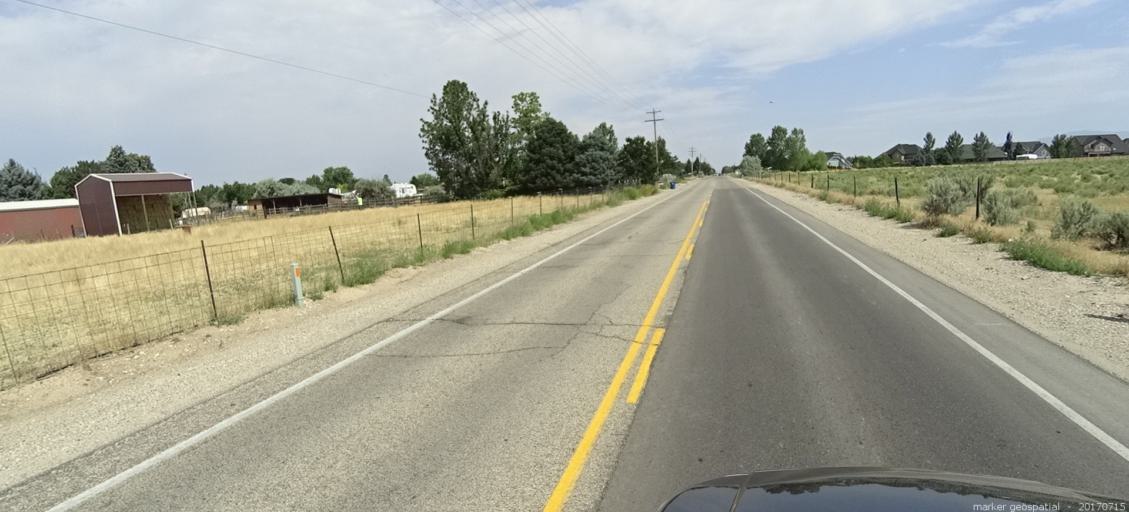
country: US
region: Idaho
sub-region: Ada County
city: Garden City
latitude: 43.5448
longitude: -116.2742
